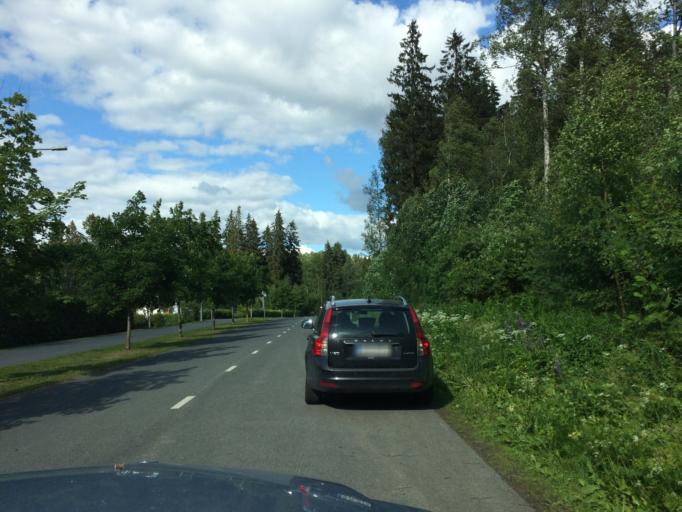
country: FI
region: Haeme
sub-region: Haemeenlinna
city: Haemeenlinna
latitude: 60.9806
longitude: 24.3950
